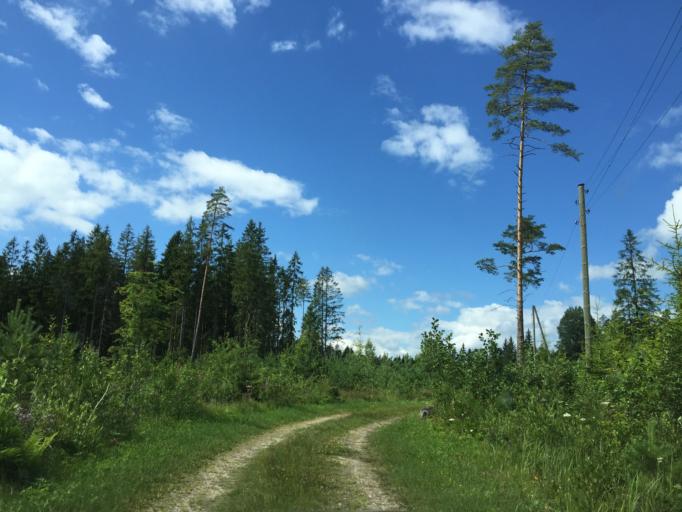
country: LV
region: Ropazu
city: Ropazi
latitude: 56.8965
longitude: 24.7182
